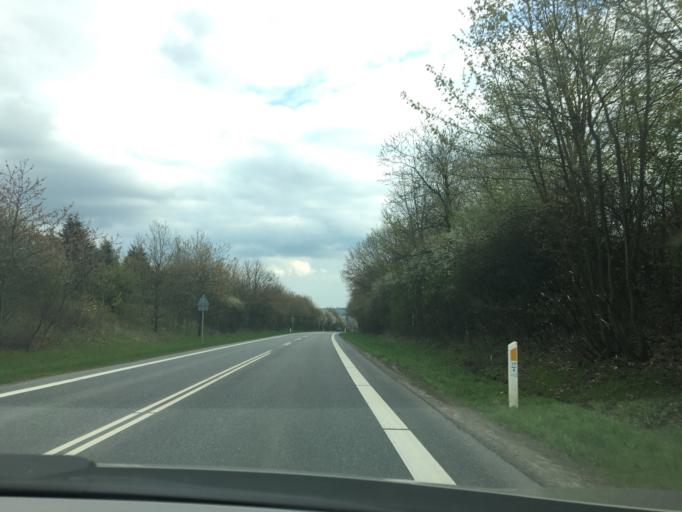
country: DK
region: Central Jutland
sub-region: Horsens Kommune
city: Braedstrup
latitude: 55.9519
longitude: 9.6304
